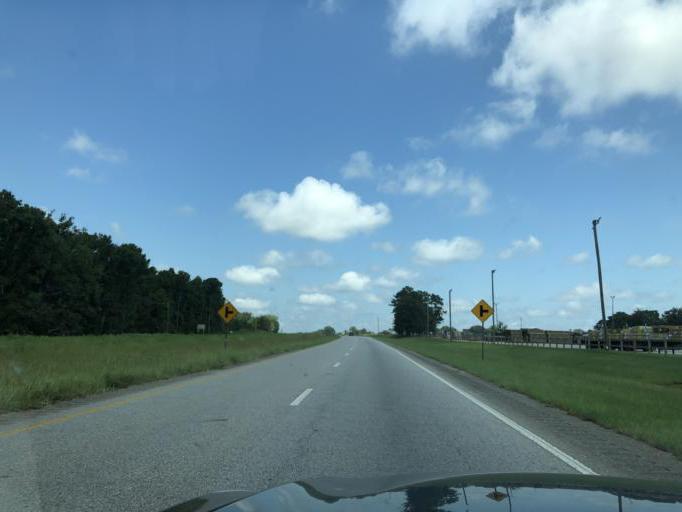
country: US
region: Alabama
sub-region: Henry County
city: Abbeville
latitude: 31.5925
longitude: -85.2776
